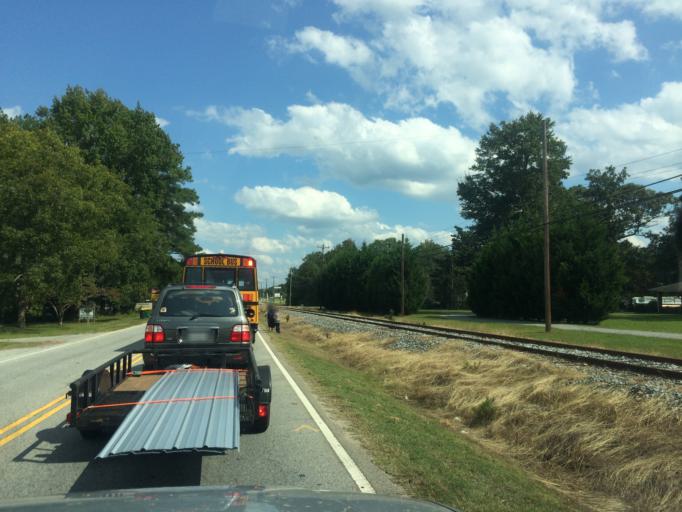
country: US
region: South Carolina
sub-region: Anderson County
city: Belton
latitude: 34.5155
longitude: -82.4840
